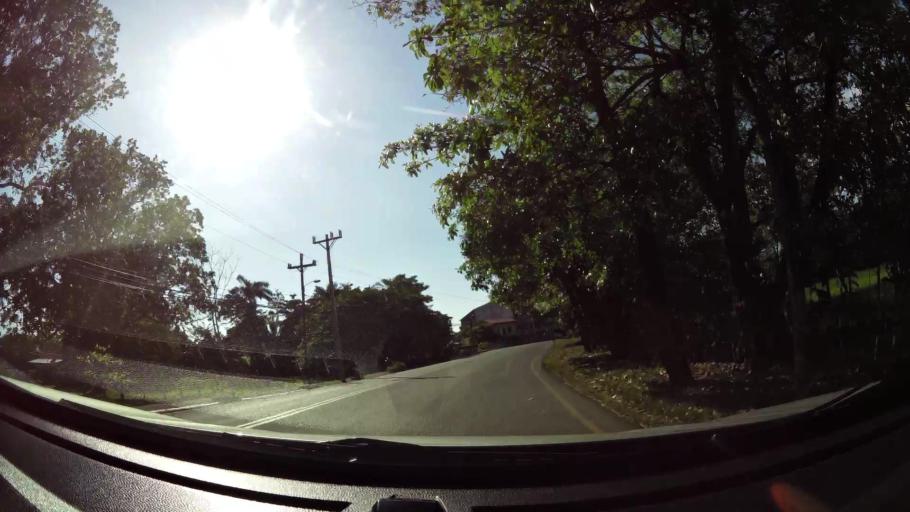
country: CR
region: Puntarenas
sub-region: Canton de Garabito
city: Jaco
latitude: 9.6101
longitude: -84.6232
